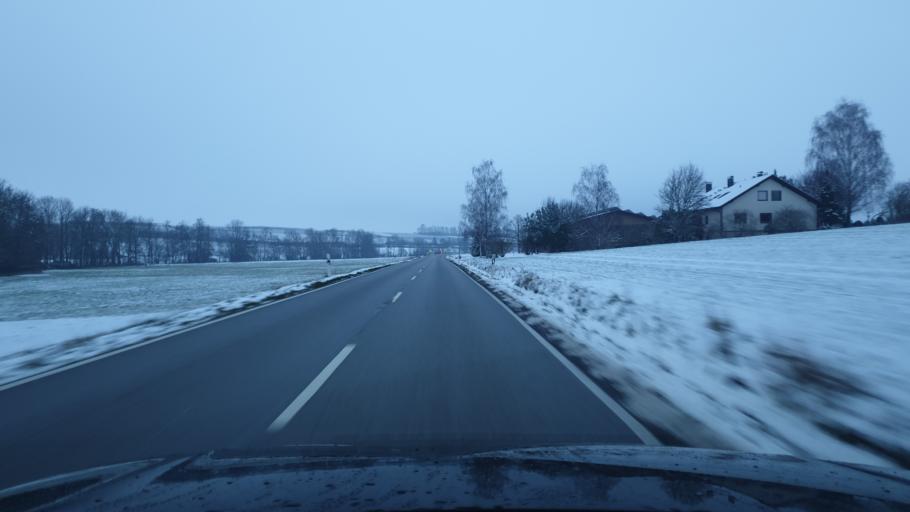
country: DE
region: Baden-Wuerttemberg
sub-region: Regierungsbezirk Stuttgart
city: Schwaigern
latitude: 49.1342
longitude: 9.0237
